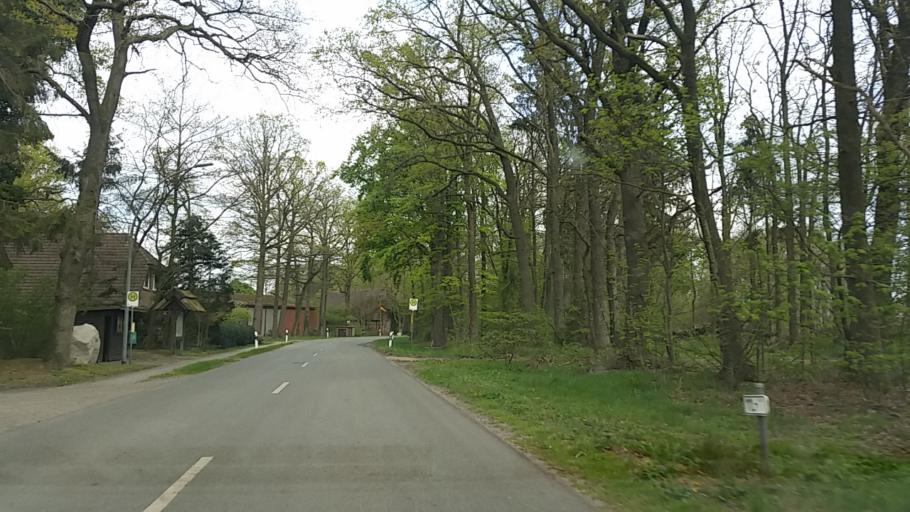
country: DE
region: Lower Saxony
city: Konigsmoor
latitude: 53.2017
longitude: 9.7066
